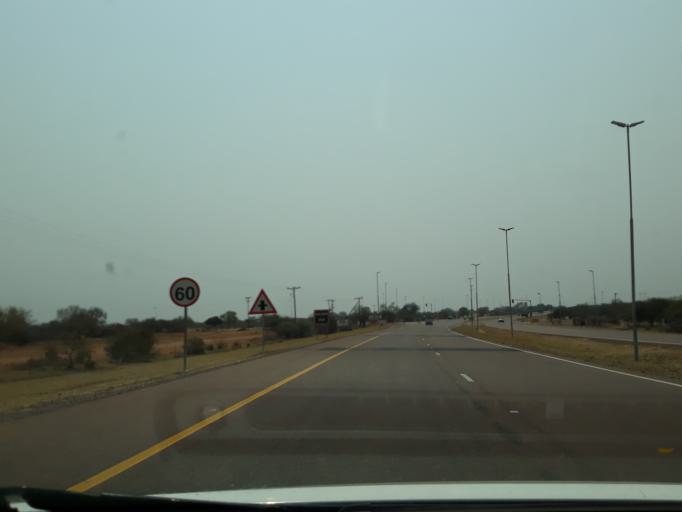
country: BW
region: Kgatleng
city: Bokaa
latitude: -24.3660
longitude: 26.0663
